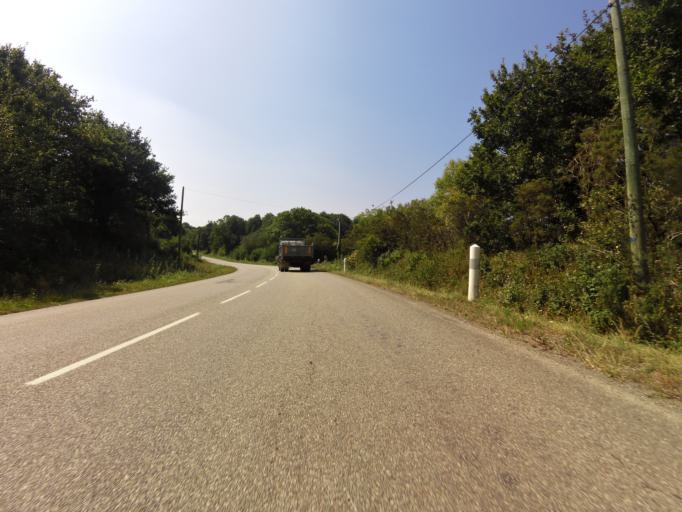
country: FR
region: Brittany
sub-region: Departement du Finistere
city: Pluguffan
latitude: 47.9450
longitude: -4.2104
